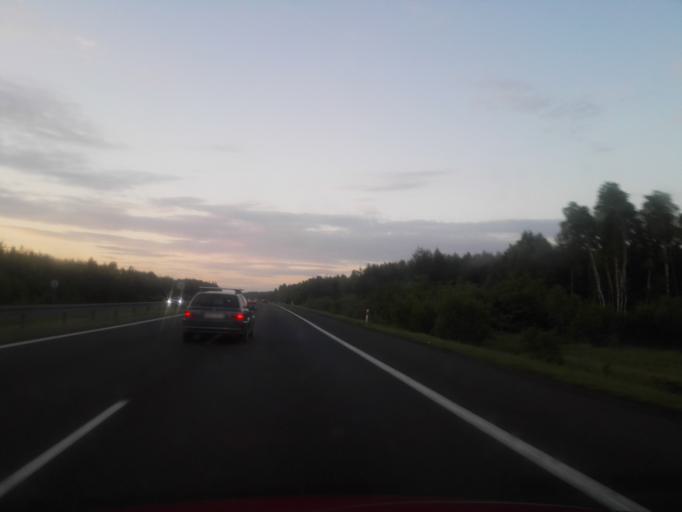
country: PL
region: Lodz Voivodeship
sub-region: Powiat radomszczanski
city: Radomsko
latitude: 51.0559
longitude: 19.3583
